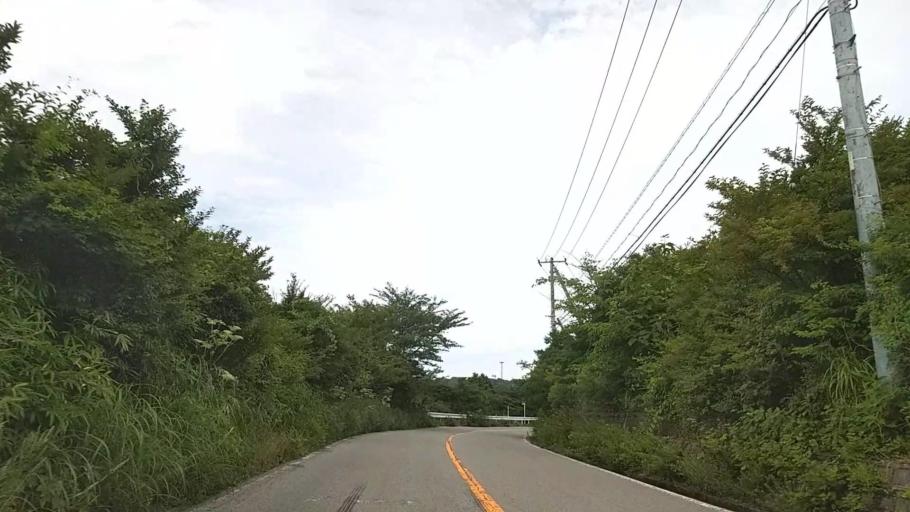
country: JP
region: Kanagawa
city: Hakone
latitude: 35.1821
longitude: 139.0592
